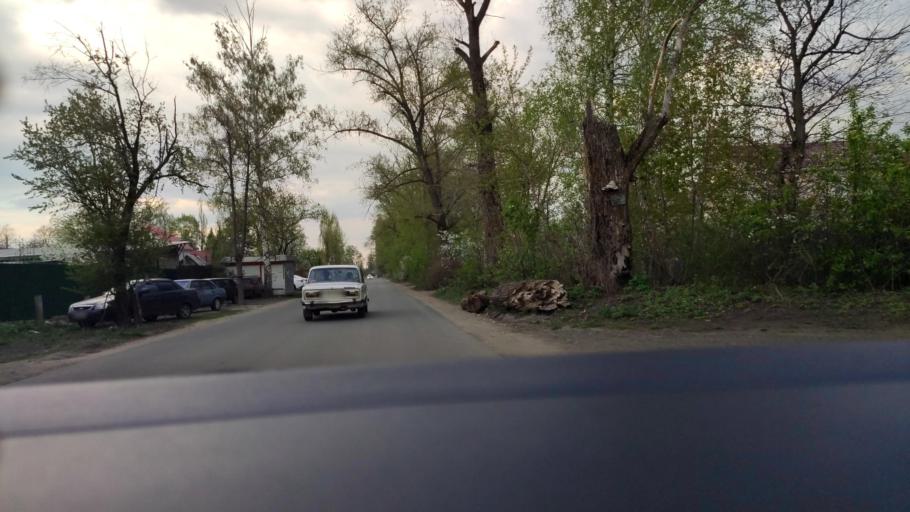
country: RU
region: Voronezj
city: Voronezh
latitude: 51.6009
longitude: 39.1638
